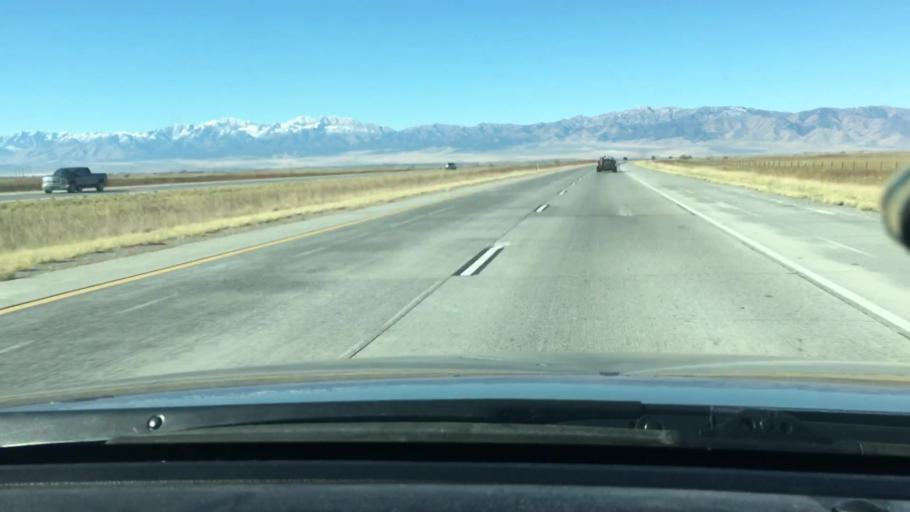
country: US
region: Utah
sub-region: Tooele County
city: Stansbury park
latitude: 40.6666
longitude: -112.3098
